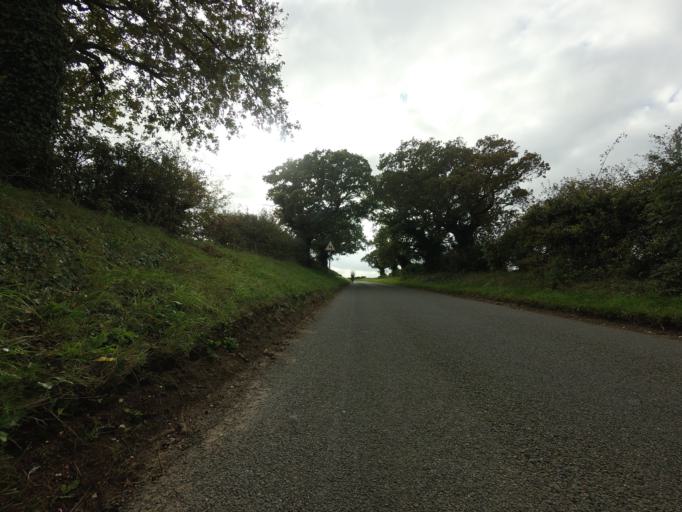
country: GB
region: England
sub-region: Norfolk
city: Snettisham
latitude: 52.8840
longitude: 0.5222
